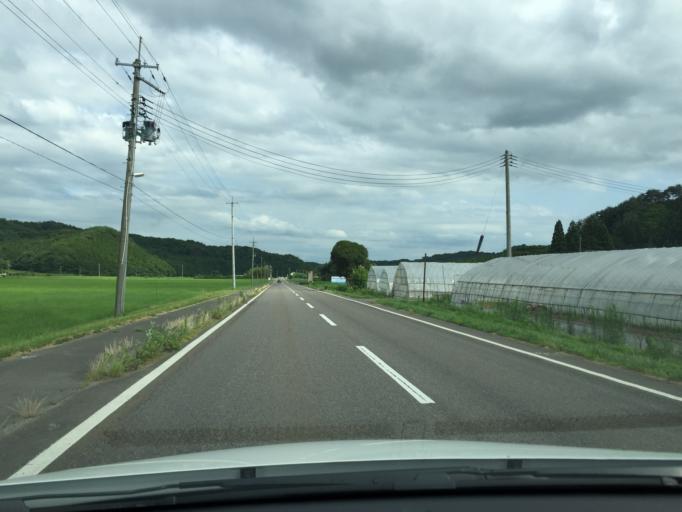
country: JP
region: Tochigi
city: Kuroiso
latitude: 37.1856
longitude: 140.1417
